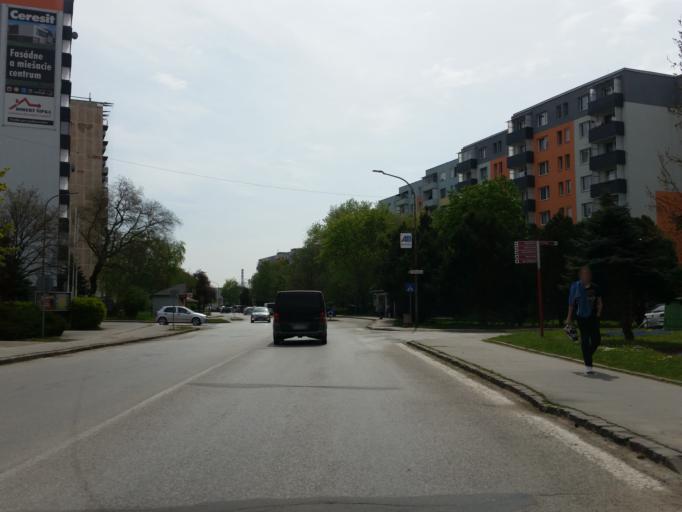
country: SK
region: Trnavsky
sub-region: Okres Galanta
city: Galanta
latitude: 48.2842
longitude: 17.7341
